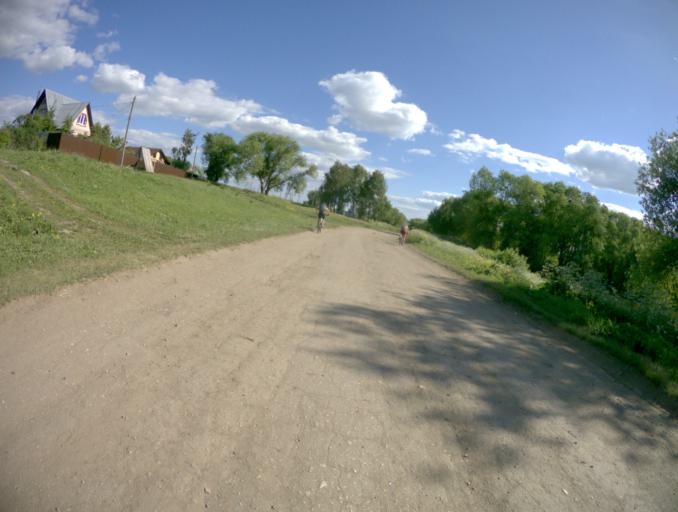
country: RU
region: Vladimir
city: Suzdal'
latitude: 56.3047
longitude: 40.2919
